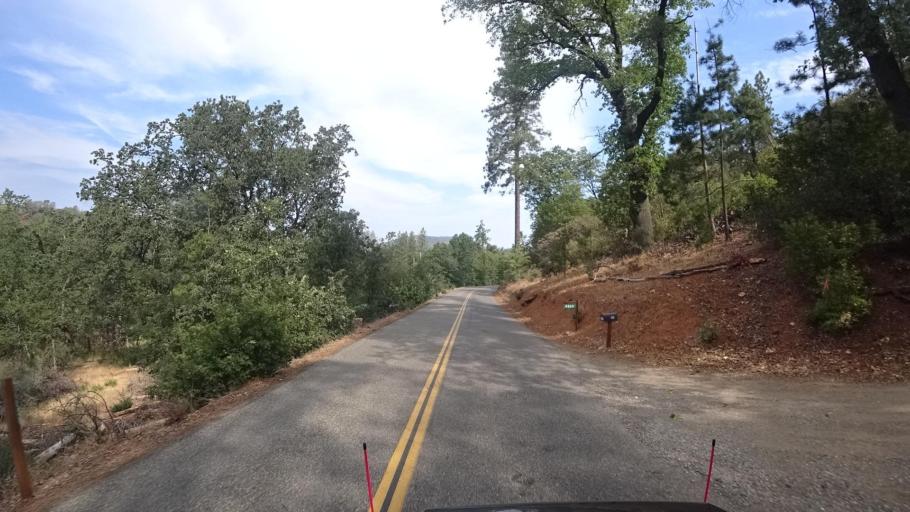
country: US
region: California
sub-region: Mariposa County
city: Midpines
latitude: 37.5168
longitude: -119.9173
